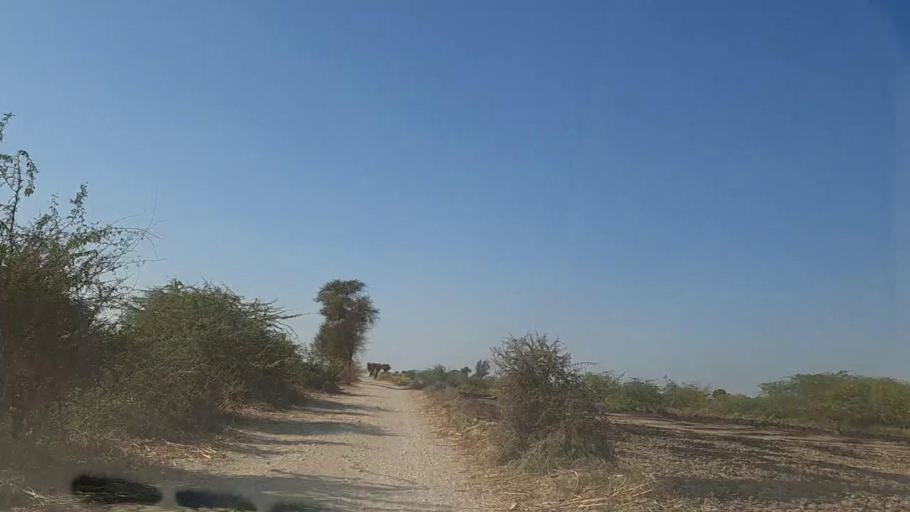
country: PK
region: Sindh
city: Digri
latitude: 25.1809
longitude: 69.0079
